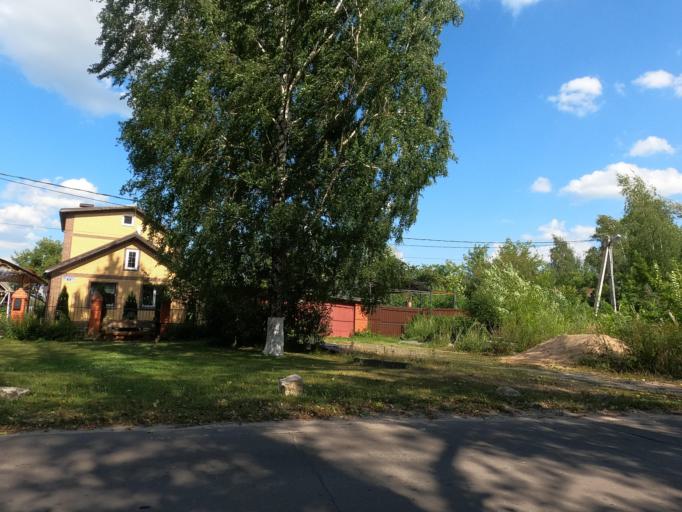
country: RU
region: Moskovskaya
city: Peski
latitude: 55.2251
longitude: 38.7518
